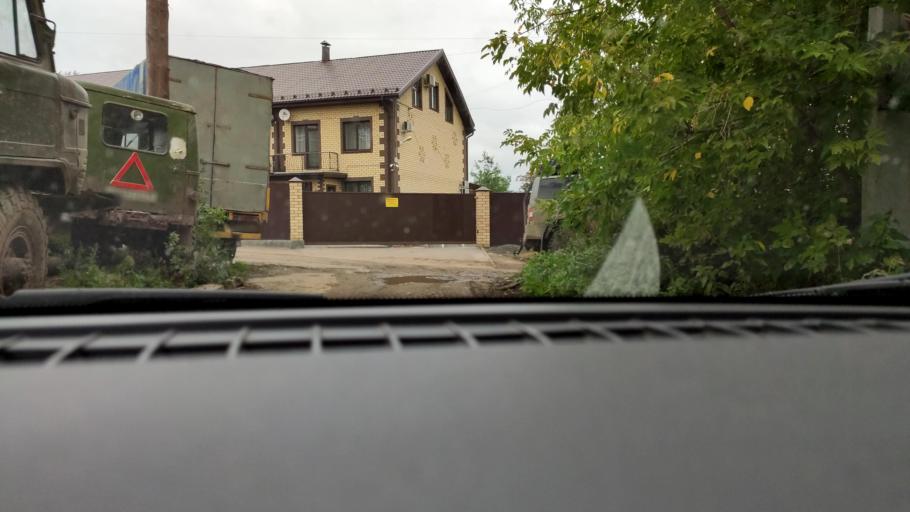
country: RU
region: Perm
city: Perm
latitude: 57.9933
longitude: 56.3102
